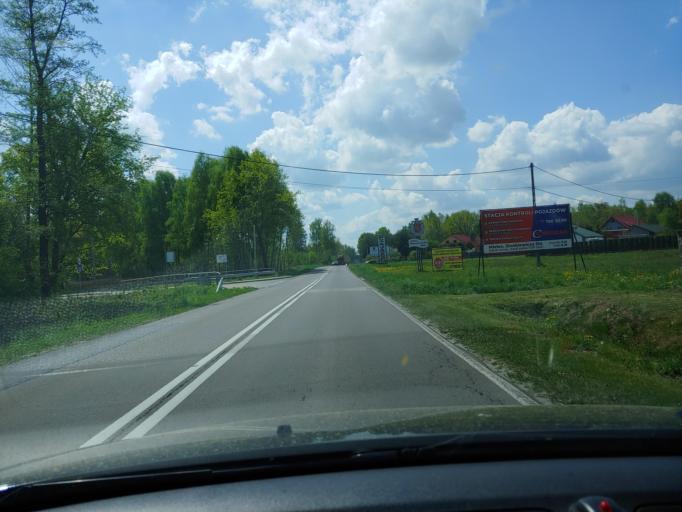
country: PL
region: Subcarpathian Voivodeship
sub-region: Powiat mielecki
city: Wadowice Gorne
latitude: 50.2542
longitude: 21.3224
